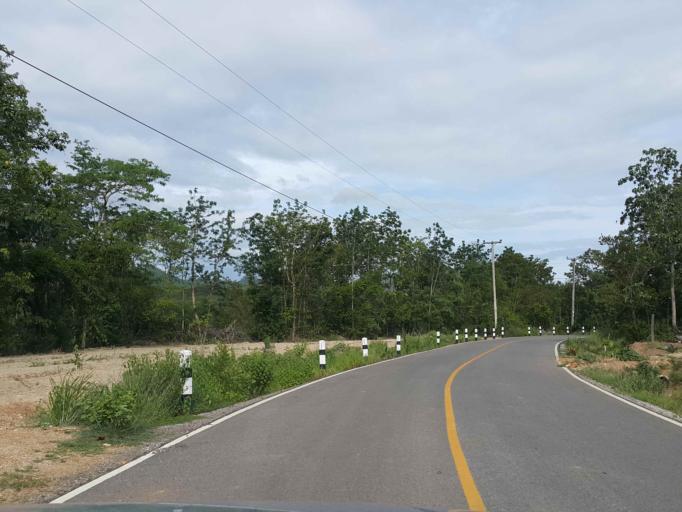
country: TH
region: Sukhothai
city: Thung Saliam
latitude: 17.2305
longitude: 99.5104
